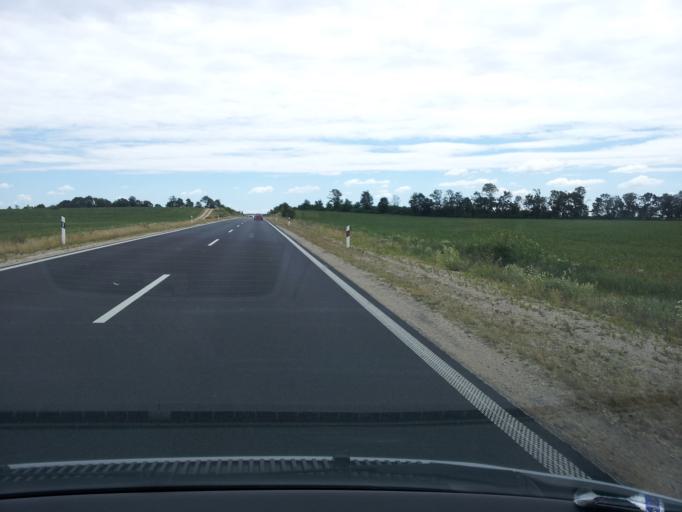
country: HU
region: Veszprem
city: Balatonkenese
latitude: 47.0638
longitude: 18.0904
